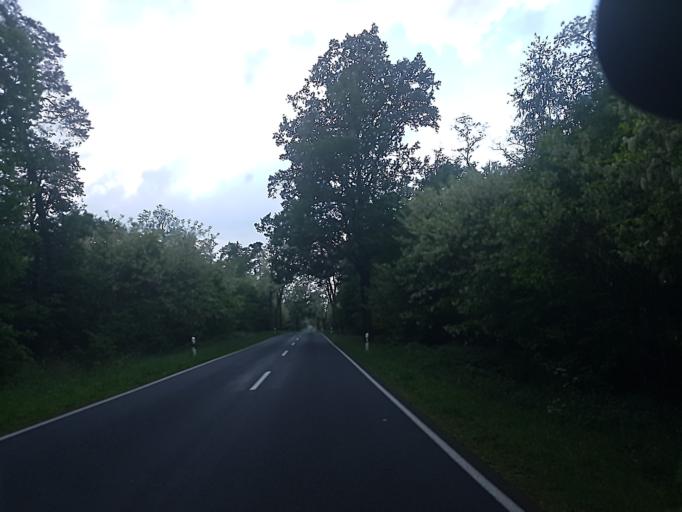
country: DE
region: Brandenburg
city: Gorzke
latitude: 52.0784
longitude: 12.3200
